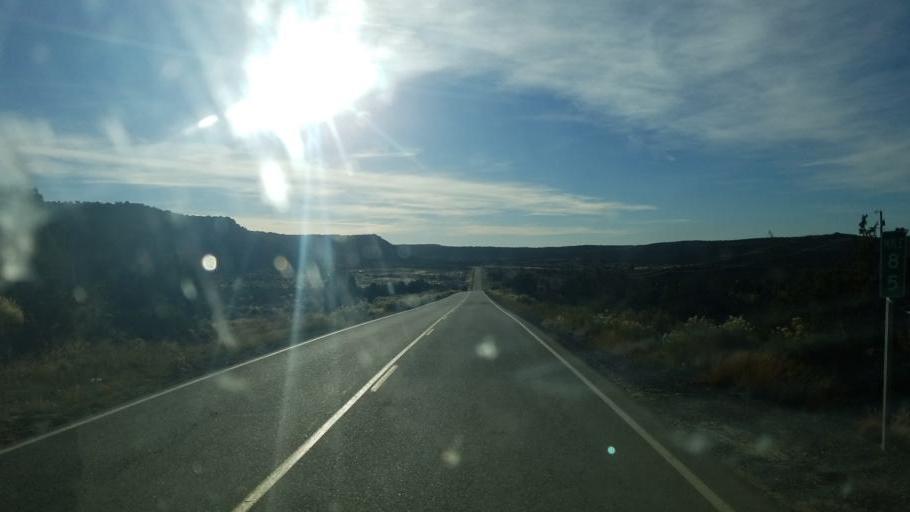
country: US
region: New Mexico
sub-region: San Juan County
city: Bloomfield
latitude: 36.7330
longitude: -107.6413
